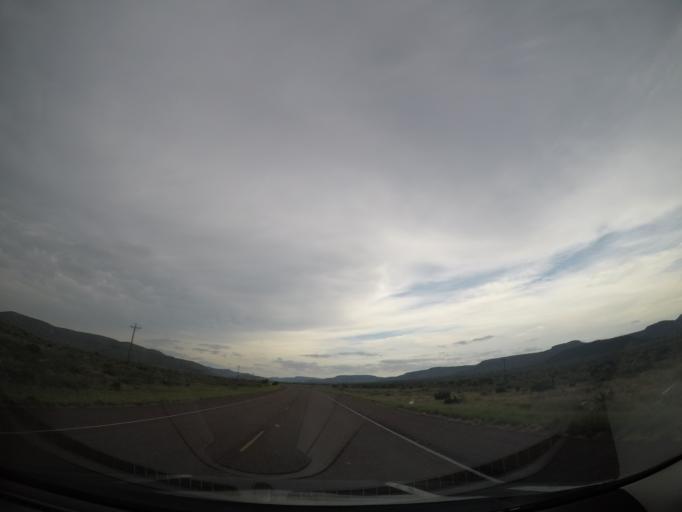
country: US
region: Texas
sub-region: Terrell County
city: Sanderson
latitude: 30.1910
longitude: -102.8821
